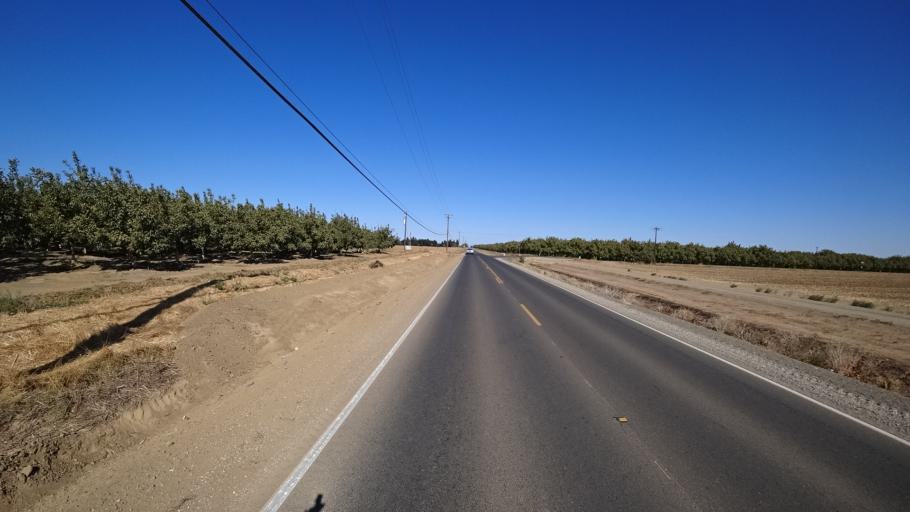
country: US
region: California
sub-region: Yolo County
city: Winters
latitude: 38.5609
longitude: -121.9713
